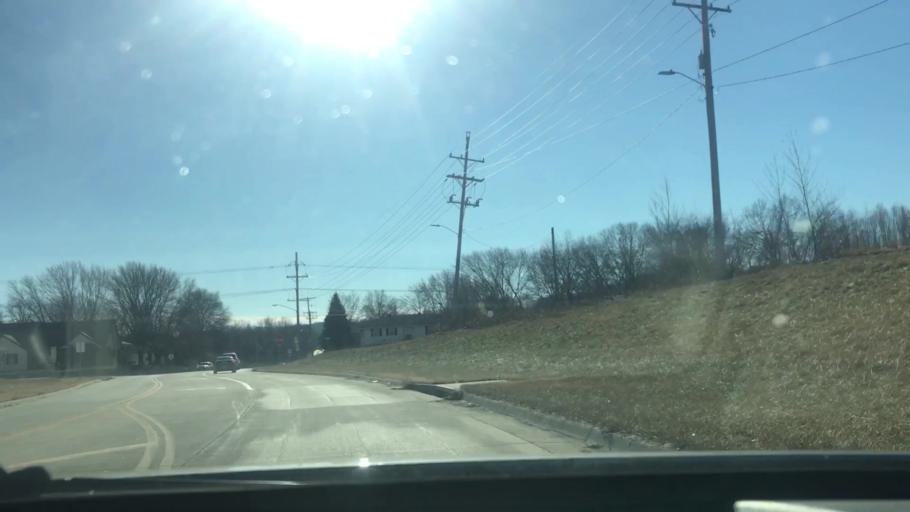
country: US
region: Kansas
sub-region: Leavenworth County
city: Leavenworth
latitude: 39.3281
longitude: -94.9507
